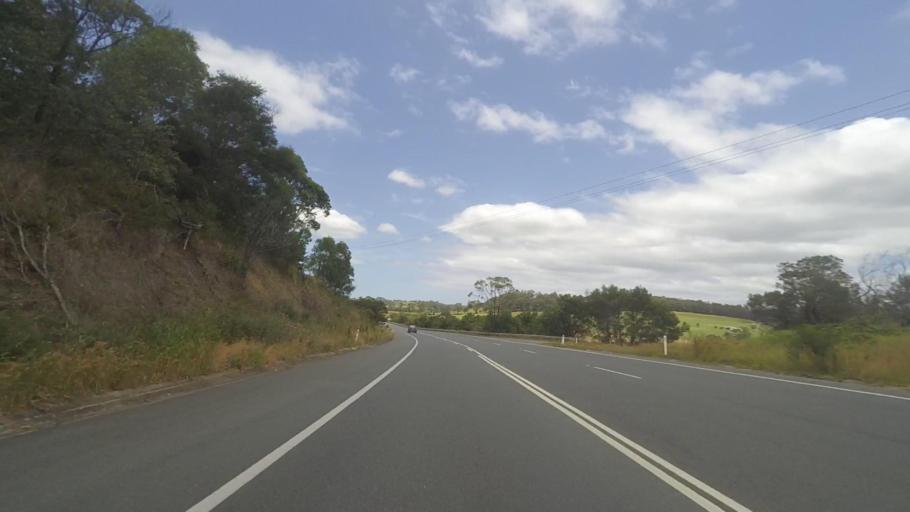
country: AU
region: New South Wales
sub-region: Shoalhaven Shire
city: Milton
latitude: -35.2654
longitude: 150.4250
